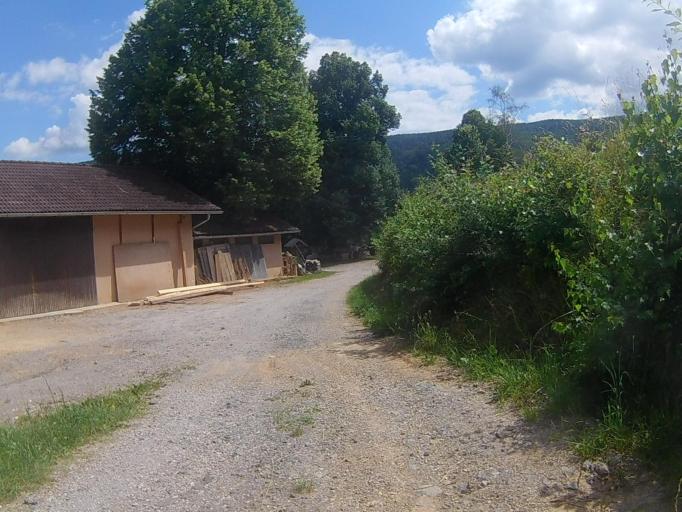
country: SI
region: Ruse
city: Ruse
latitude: 46.5186
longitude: 15.5209
